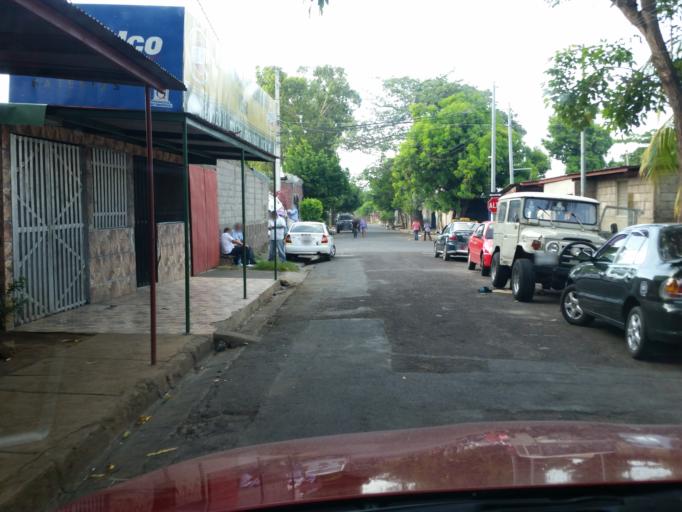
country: NI
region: Managua
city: Managua
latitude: 12.1484
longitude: -86.2787
